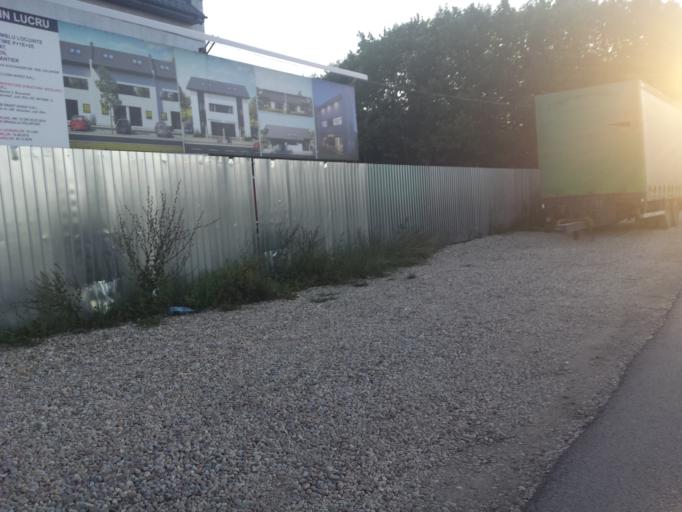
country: RO
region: Ilfov
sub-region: Comuna Tunari
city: Tunari
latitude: 44.5159
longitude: 26.1490
